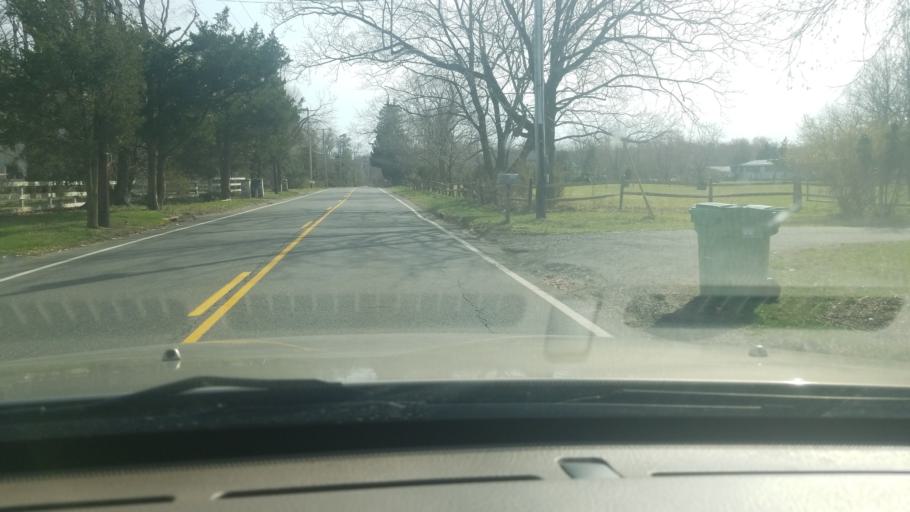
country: US
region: New Jersey
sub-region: Ocean County
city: Cedar Glen West
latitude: 40.0650
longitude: -74.2732
